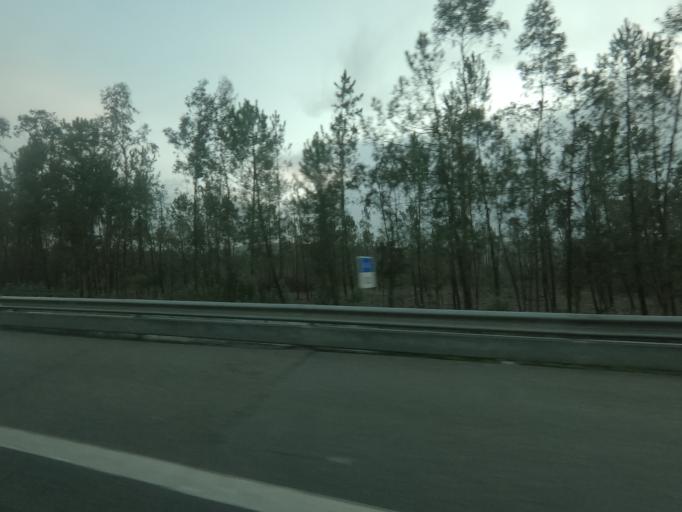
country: PT
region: Braga
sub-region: Barcelos
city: Galegos
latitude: 41.6487
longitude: -8.5515
